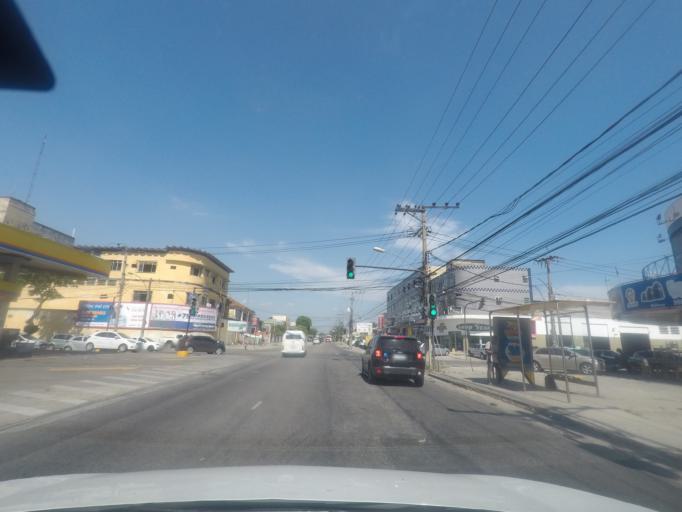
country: BR
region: Rio de Janeiro
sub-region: Nilopolis
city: Nilopolis
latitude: -22.8796
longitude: -43.4565
